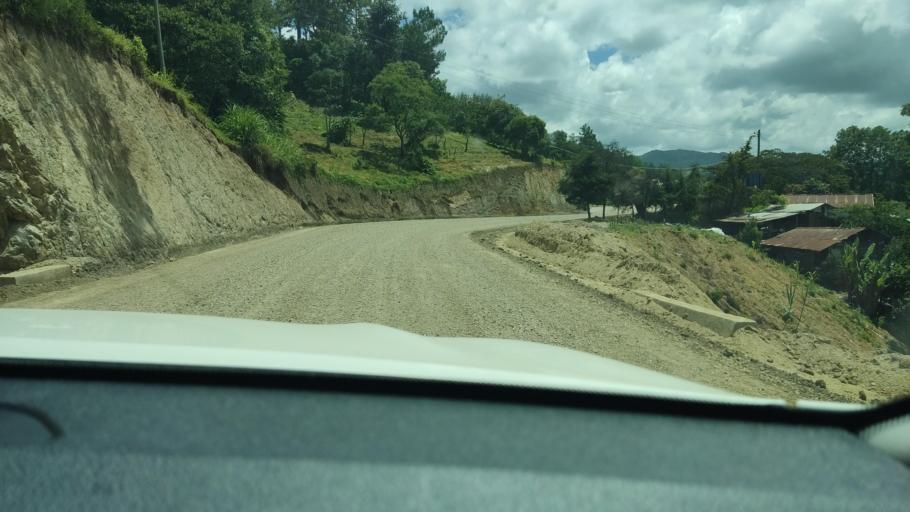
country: GT
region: Chimaltenango
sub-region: Municipio de San Juan Comalapa
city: Comalapa
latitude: 14.7890
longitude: -90.8593
